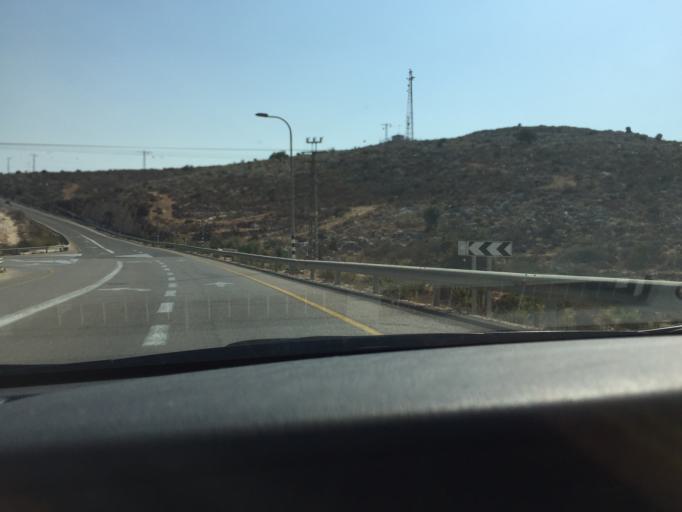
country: PS
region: West Bank
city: Sartah
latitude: 32.0907
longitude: 35.1032
